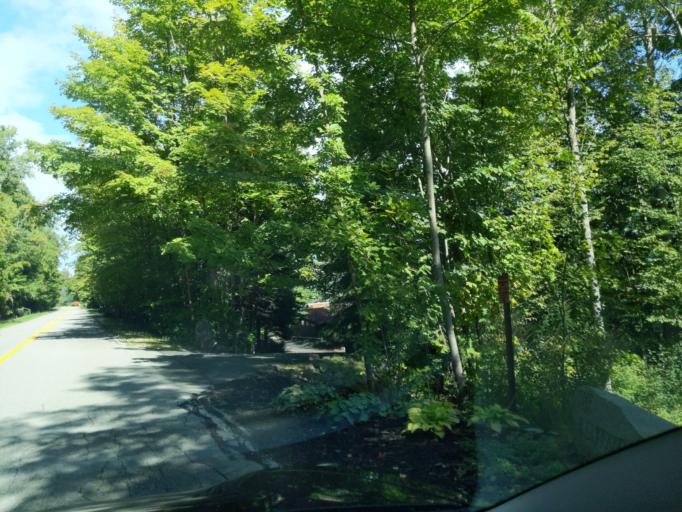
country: US
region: Michigan
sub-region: Antrim County
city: Elk Rapids
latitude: 44.9521
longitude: -85.3223
